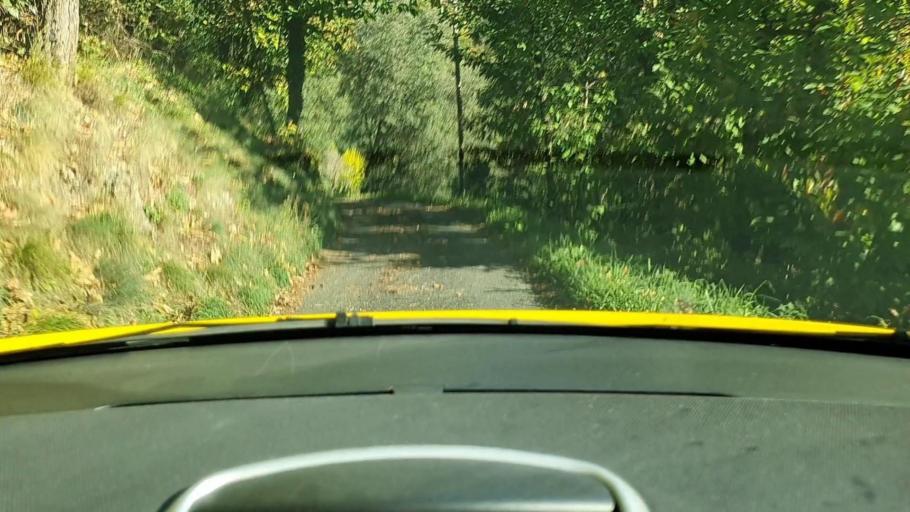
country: FR
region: Languedoc-Roussillon
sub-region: Departement du Gard
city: Sumene
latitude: 44.0667
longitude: 3.7299
